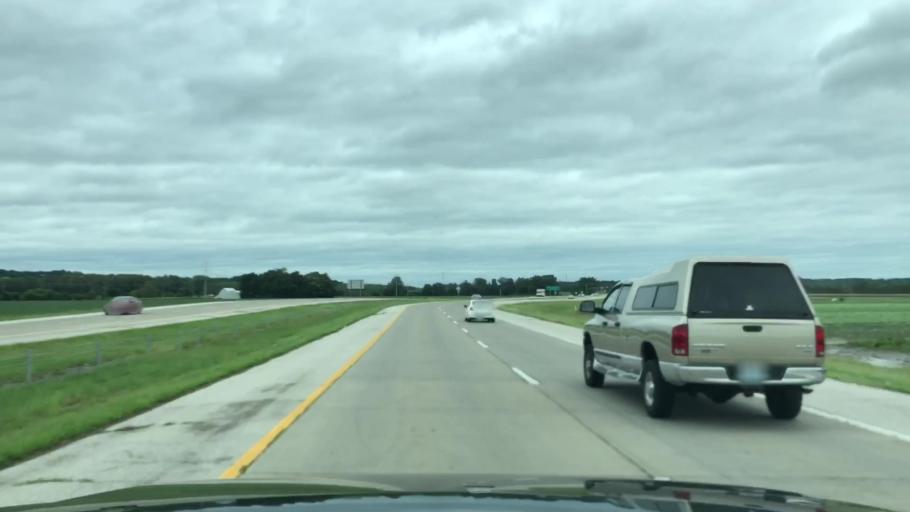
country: US
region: Missouri
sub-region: Saint Charles County
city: Saint Charles
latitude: 38.7220
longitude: -90.4983
